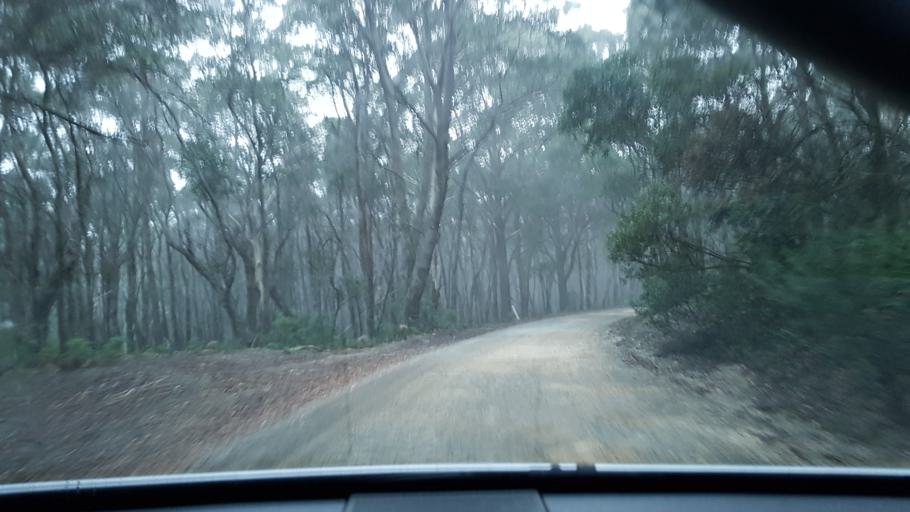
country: AU
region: New South Wales
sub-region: Blue Mountains Municipality
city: Katoomba
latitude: -33.9938
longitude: 150.0734
